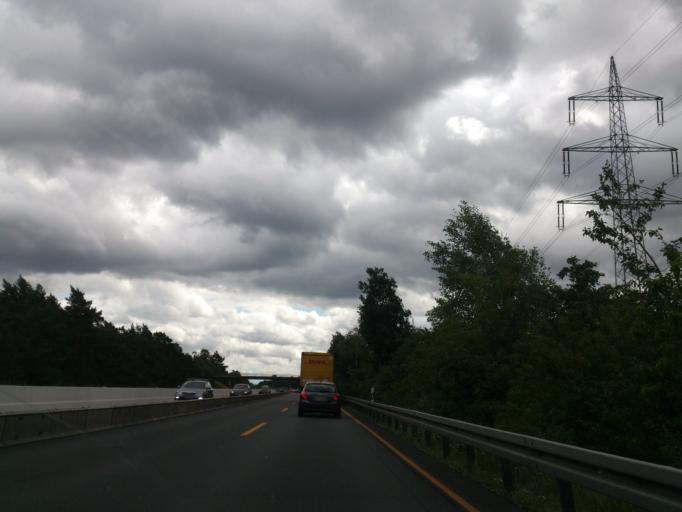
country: DE
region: North Rhine-Westphalia
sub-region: Regierungsbezirk Detmold
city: Hovelhof
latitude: 51.8448
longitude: 8.6766
